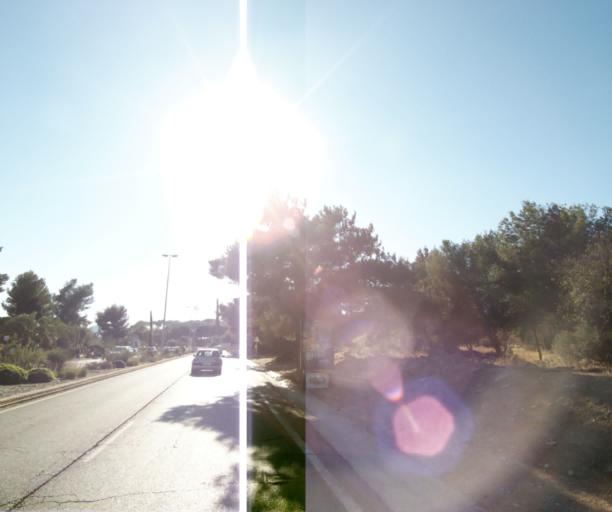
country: FR
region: Provence-Alpes-Cote d'Azur
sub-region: Departement des Bouches-du-Rhone
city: La Ciotat
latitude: 43.1910
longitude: 5.6043
